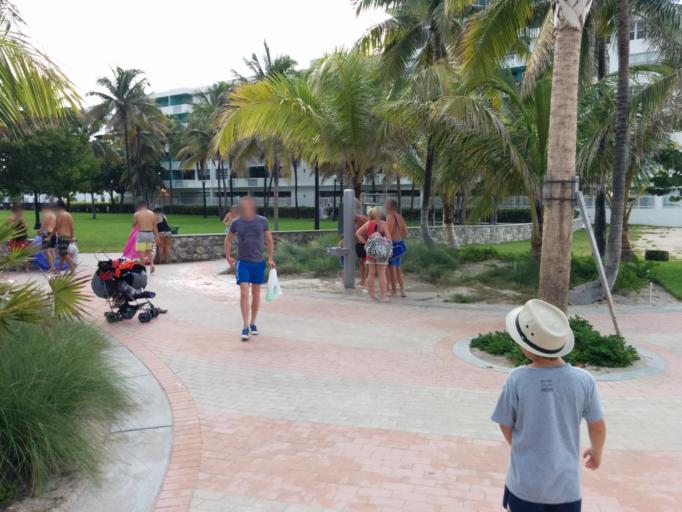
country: US
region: Florida
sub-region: Miami-Dade County
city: Miami Beach
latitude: 25.7714
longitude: -80.1314
